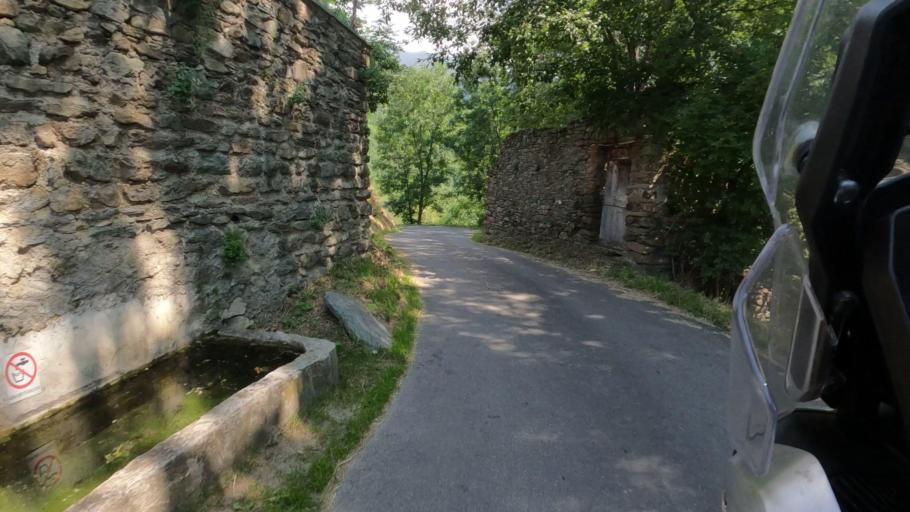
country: IT
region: Piedmont
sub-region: Provincia di Torino
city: Sant'Antonino di Susa
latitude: 45.1465
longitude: 7.2799
